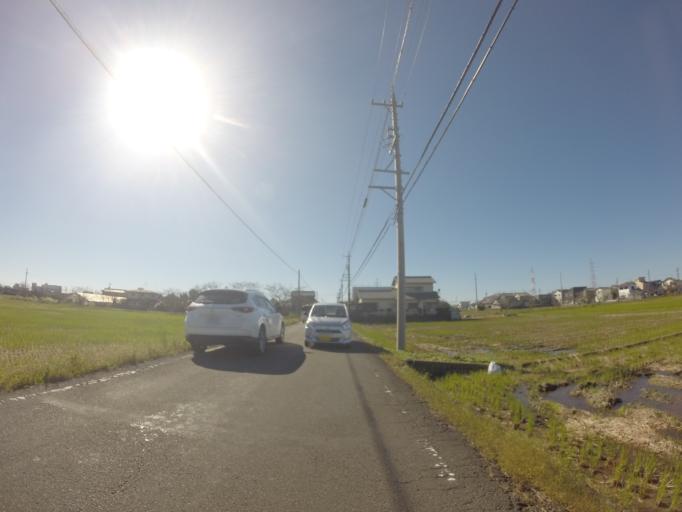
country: JP
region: Shizuoka
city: Fujieda
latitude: 34.8310
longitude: 138.2390
